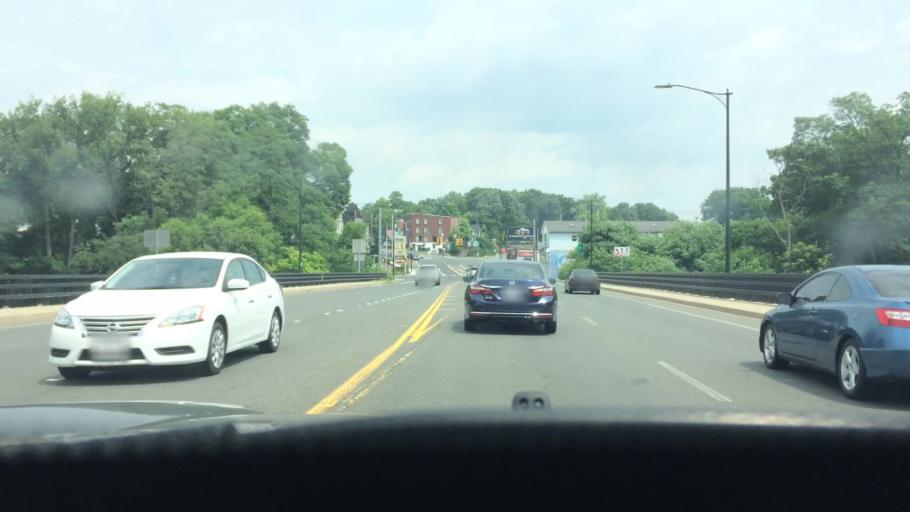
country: US
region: Massachusetts
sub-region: Hampden County
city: Chicopee
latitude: 42.1595
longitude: -72.5819
